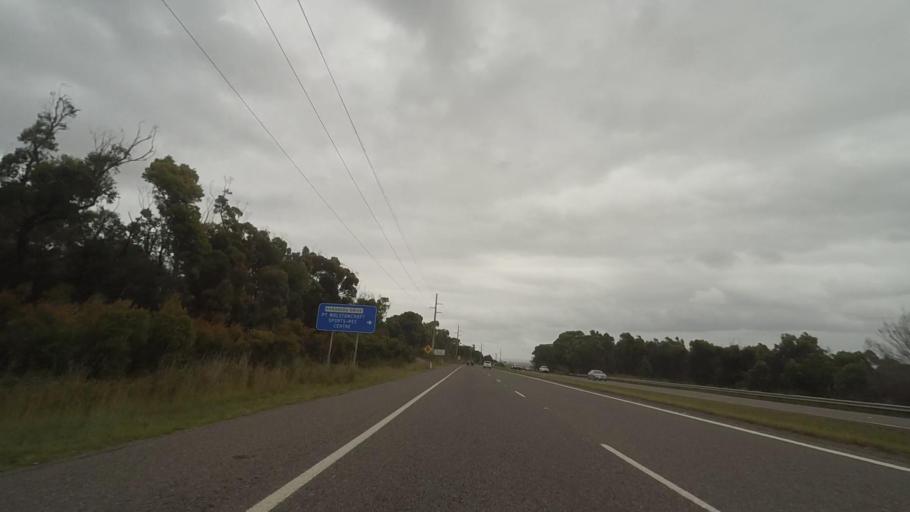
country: AU
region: New South Wales
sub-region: Wyong Shire
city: Kingfisher Shores
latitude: -33.1796
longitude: 151.5981
